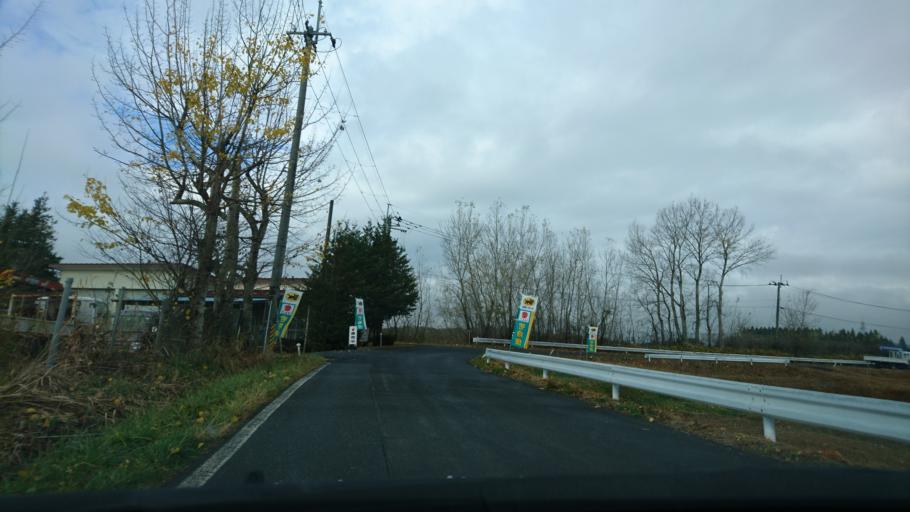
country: JP
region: Iwate
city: Ichinoseki
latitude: 38.8880
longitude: 141.1924
